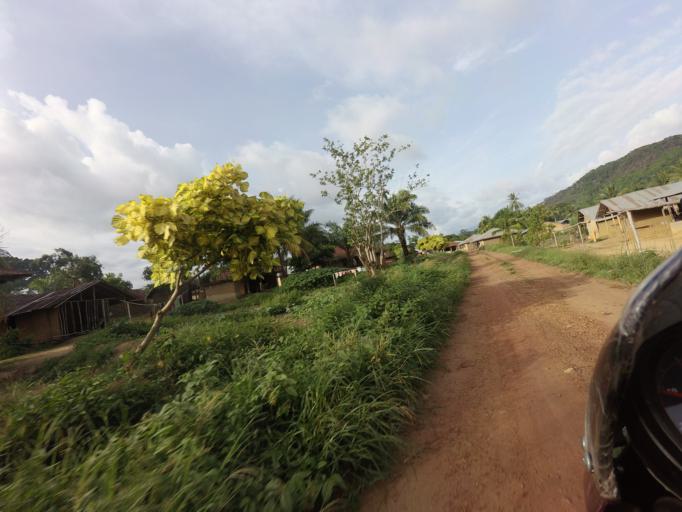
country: SL
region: Eastern Province
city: Jojoima
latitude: 7.8500
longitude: -10.8073
